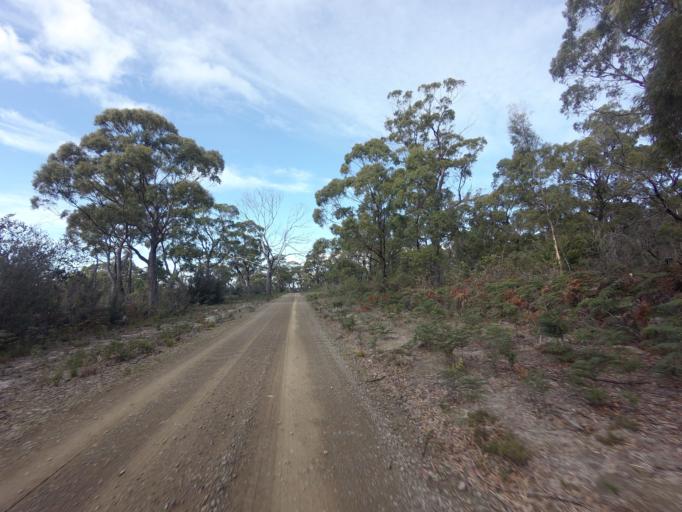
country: AU
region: Tasmania
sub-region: Clarence
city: Sandford
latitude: -42.9799
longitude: 147.7187
